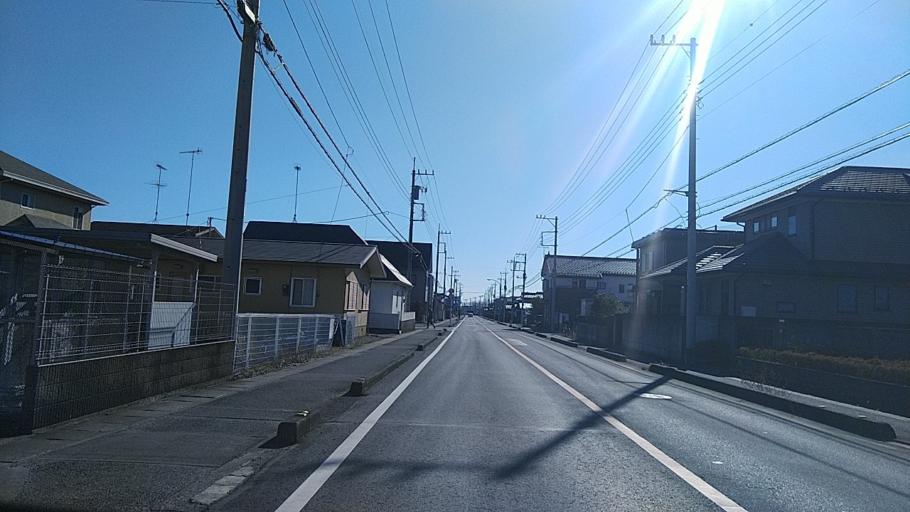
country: JP
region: Tochigi
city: Tanuma
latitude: 36.3537
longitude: 139.5568
